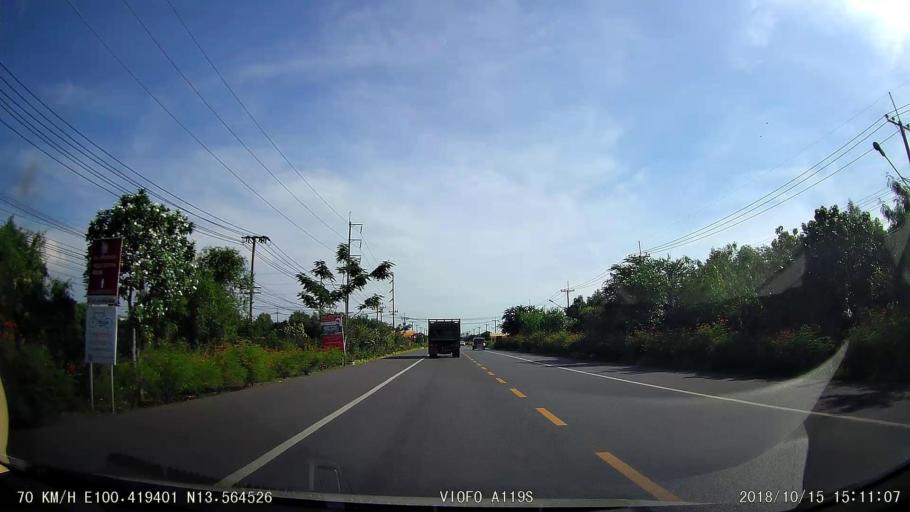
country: TH
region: Bangkok
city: Bang Khun Thian
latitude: 13.5644
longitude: 100.4194
